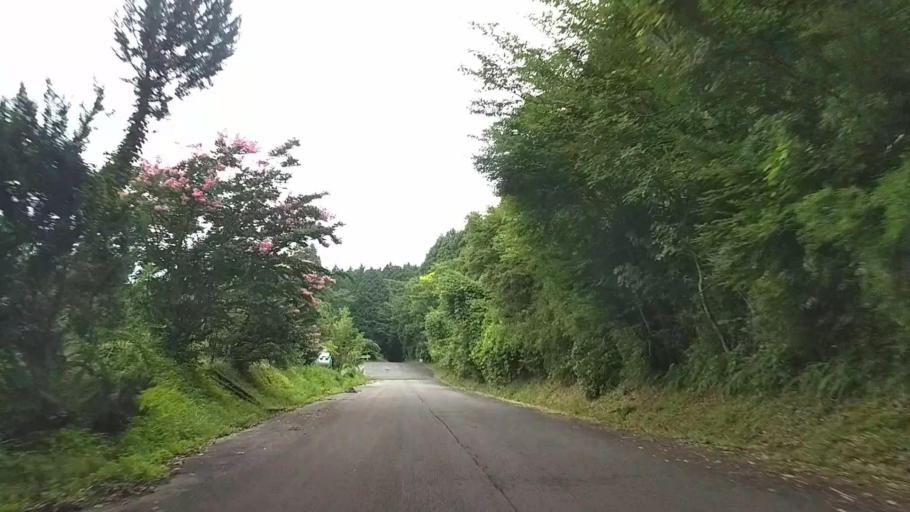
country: JP
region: Shizuoka
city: Gotemba
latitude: 35.3275
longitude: 138.9907
